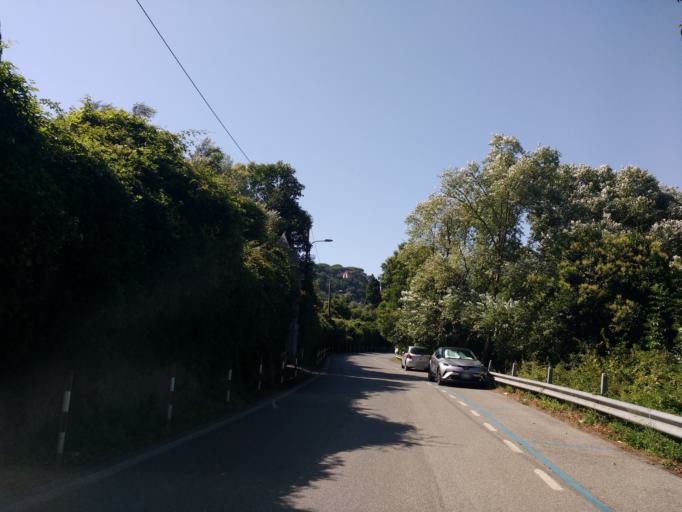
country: IT
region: Latium
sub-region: Citta metropolitana di Roma Capitale
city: Castel Gandolfo
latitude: 41.7484
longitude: 12.6545
